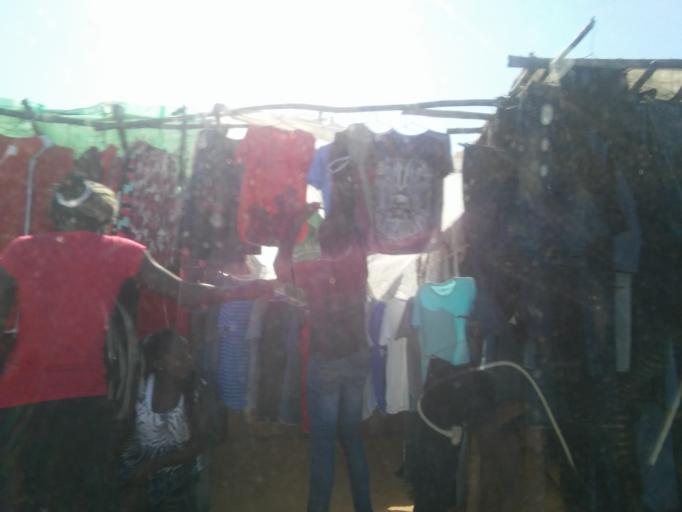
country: MZ
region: Maputo City
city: Maputo
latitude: -25.8311
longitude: 32.5746
